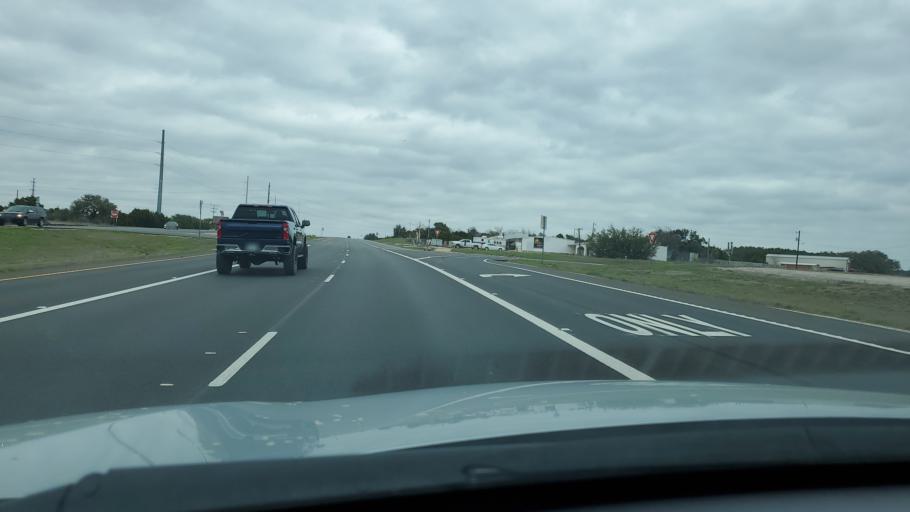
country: US
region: Texas
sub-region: Williamson County
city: Florence
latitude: 30.9800
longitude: -97.7717
